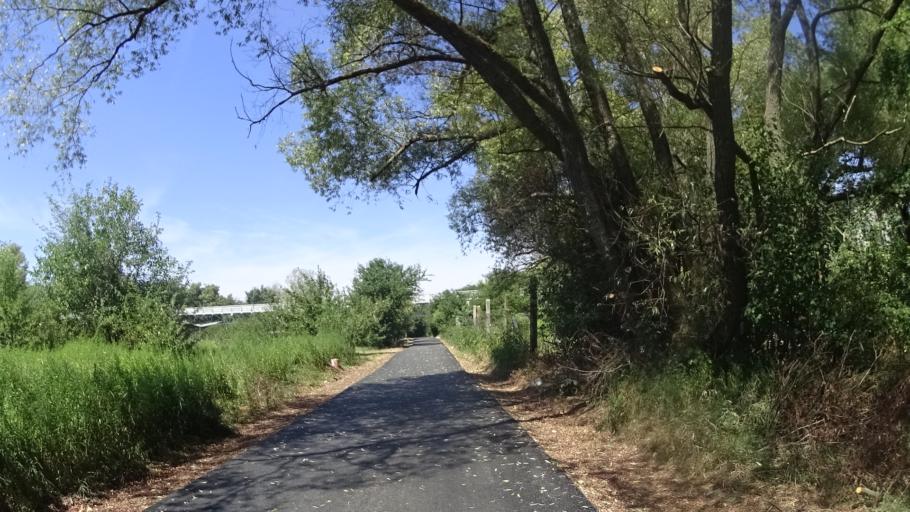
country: AT
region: Lower Austria
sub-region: Politischer Bezirk Bruck an der Leitha
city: Hainburg an der Donau
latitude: 48.2099
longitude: 16.9688
